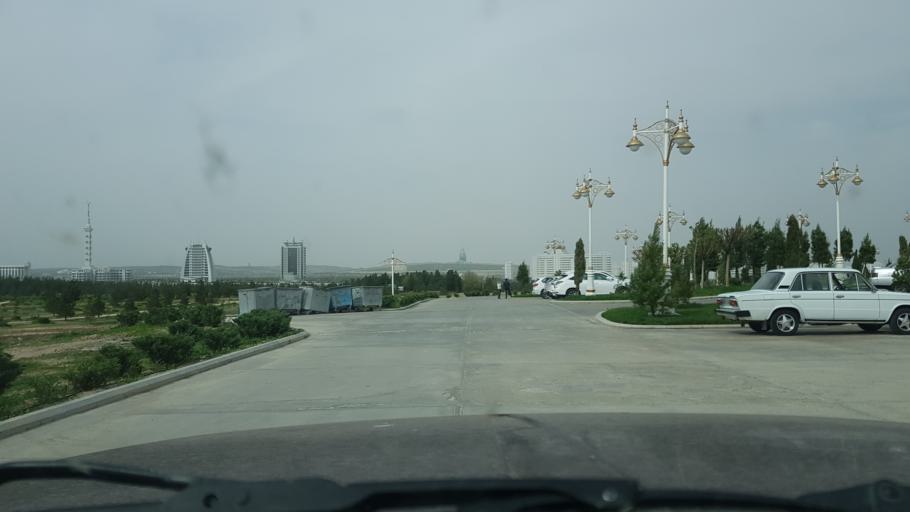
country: TM
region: Ahal
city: Ashgabat
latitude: 37.8823
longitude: 58.3298
